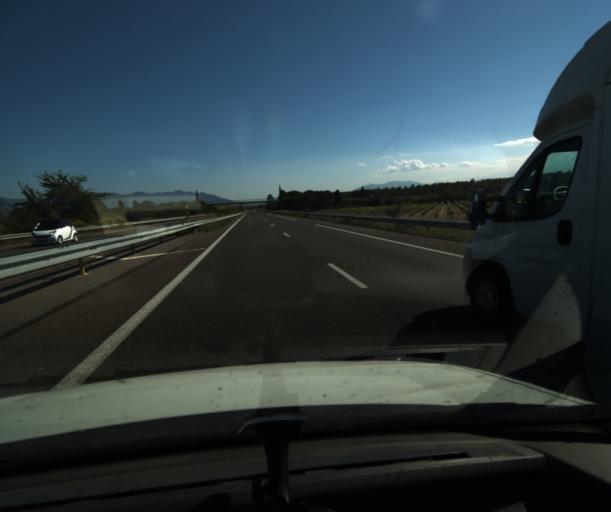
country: FR
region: Languedoc-Roussillon
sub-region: Departement des Pyrenees-Orientales
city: Pollestres
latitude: 42.6413
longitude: 2.8609
